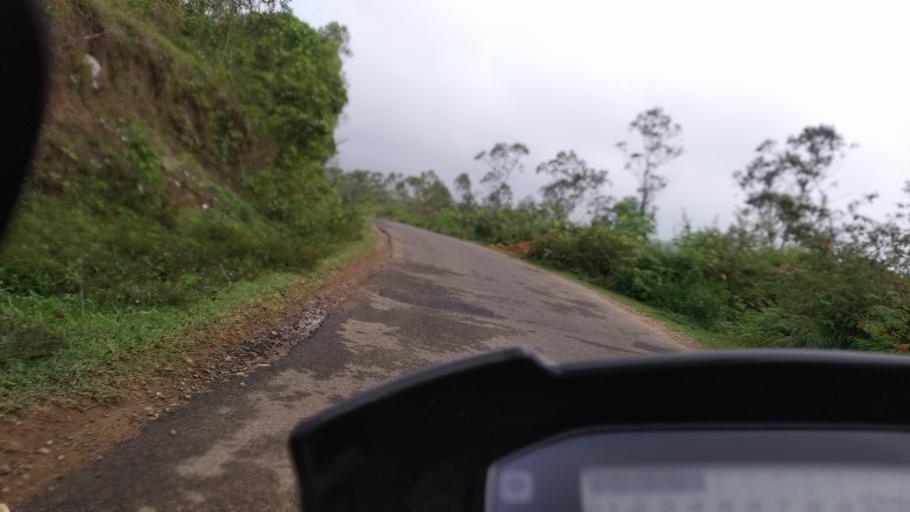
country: IN
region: Kerala
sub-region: Kottayam
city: Erattupetta
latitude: 9.5888
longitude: 77.0074
